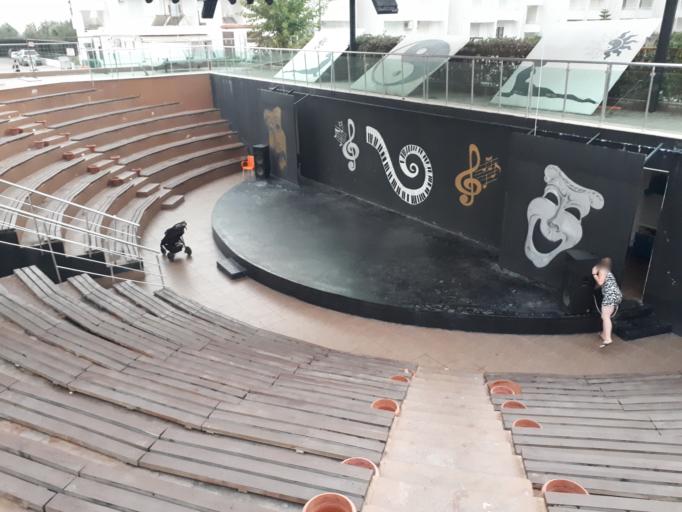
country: TR
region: Antalya
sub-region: Alanya
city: Payallar
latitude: 36.5847
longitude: 31.8714
